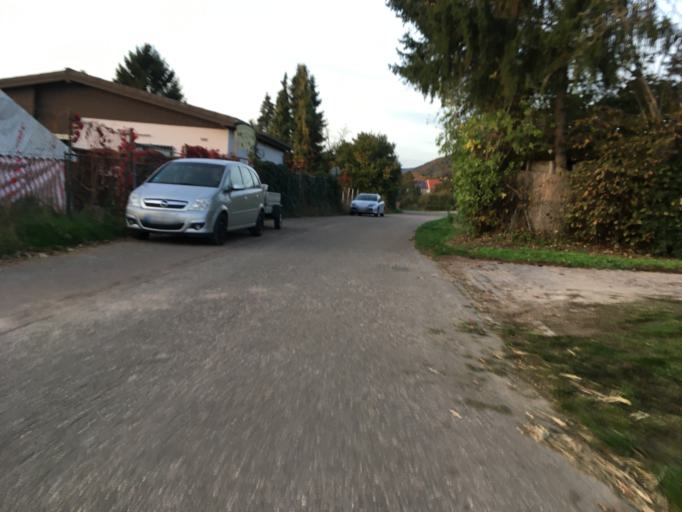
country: DE
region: Baden-Wuerttemberg
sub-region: Karlsruhe Region
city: Leimen
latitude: 49.3696
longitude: 8.6911
